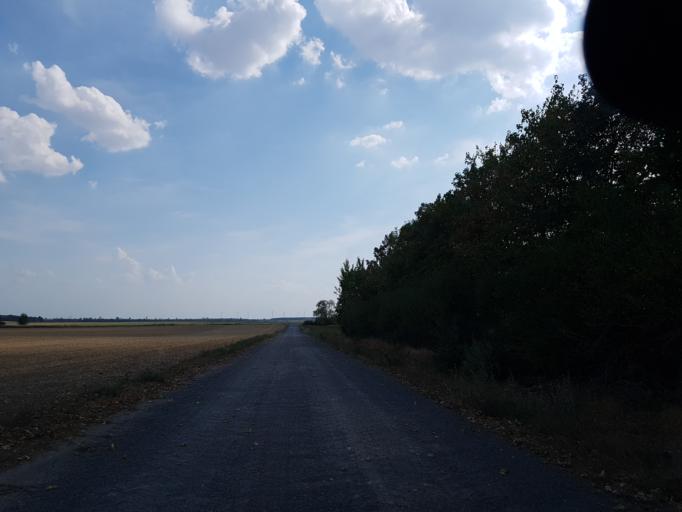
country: DE
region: Brandenburg
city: Treuenbrietzen
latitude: 51.9928
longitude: 12.8687
